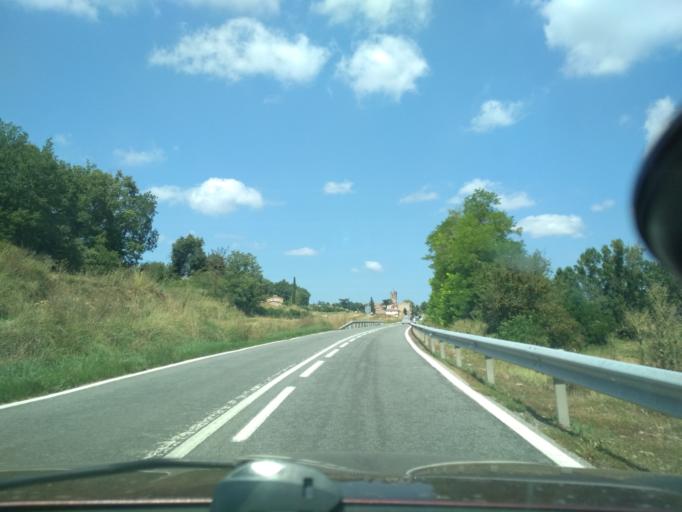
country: ES
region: Catalonia
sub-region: Provincia de Barcelona
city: Castelltercol
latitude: 41.7461
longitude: 2.1275
